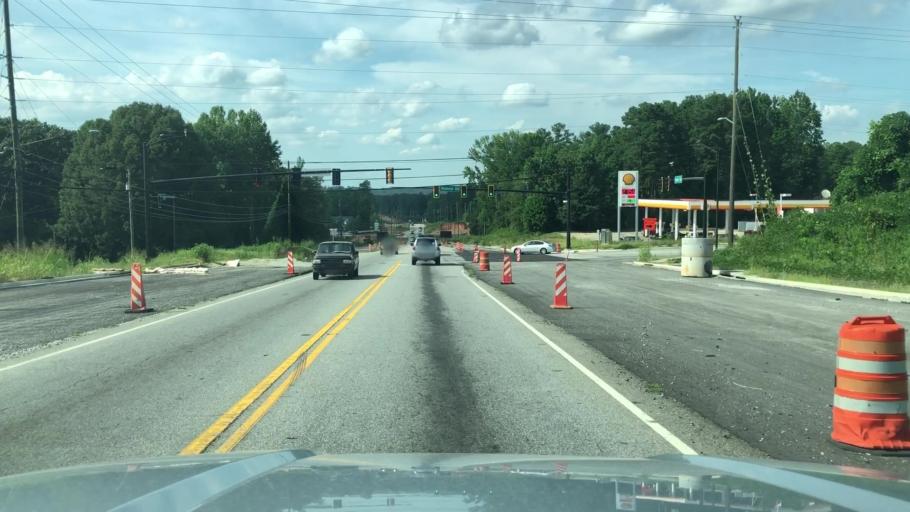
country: US
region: Georgia
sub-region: Douglas County
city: Douglasville
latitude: 33.7694
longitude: -84.7481
